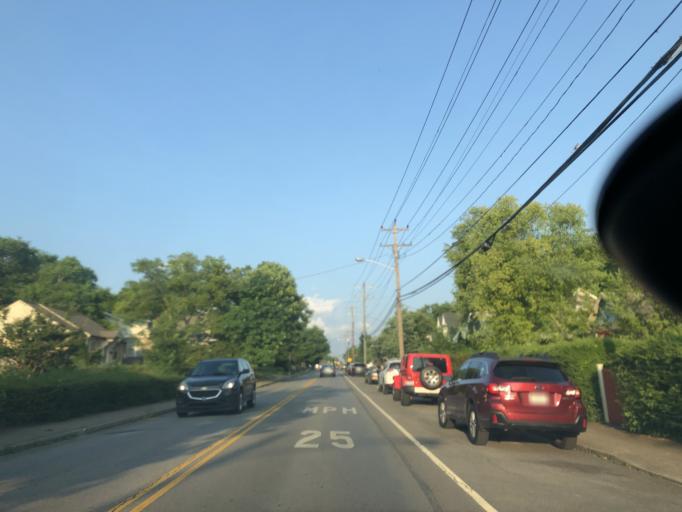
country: US
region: Tennessee
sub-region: Davidson County
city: Nashville
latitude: 36.1308
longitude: -86.8058
